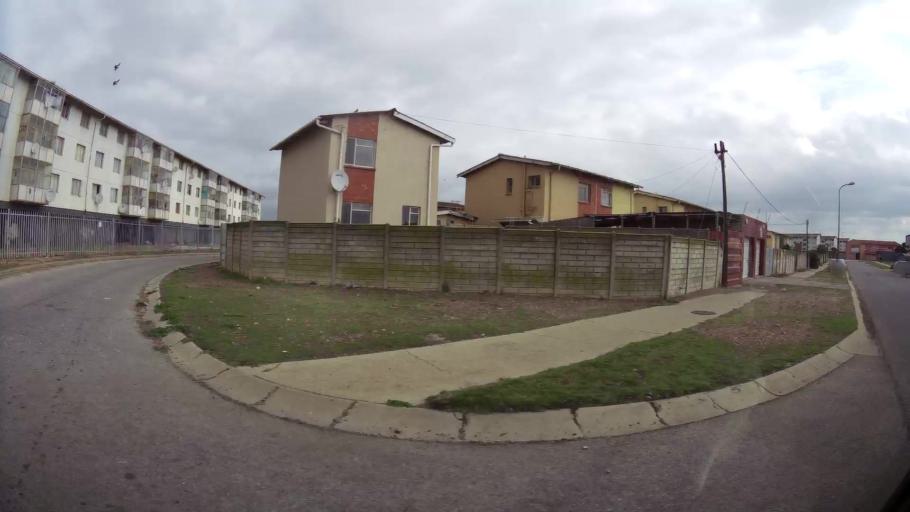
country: ZA
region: Eastern Cape
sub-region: Nelson Mandela Bay Metropolitan Municipality
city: Port Elizabeth
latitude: -33.8951
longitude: 25.5591
